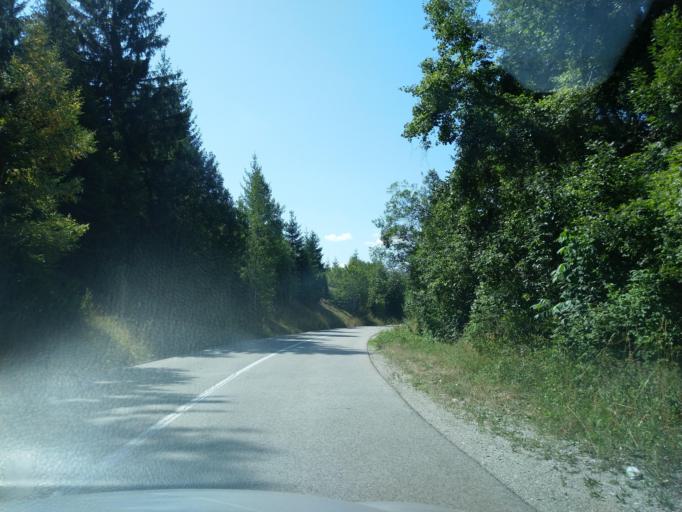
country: RS
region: Central Serbia
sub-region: Zlatiborski Okrug
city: Nova Varos
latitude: 43.3497
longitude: 19.8537
